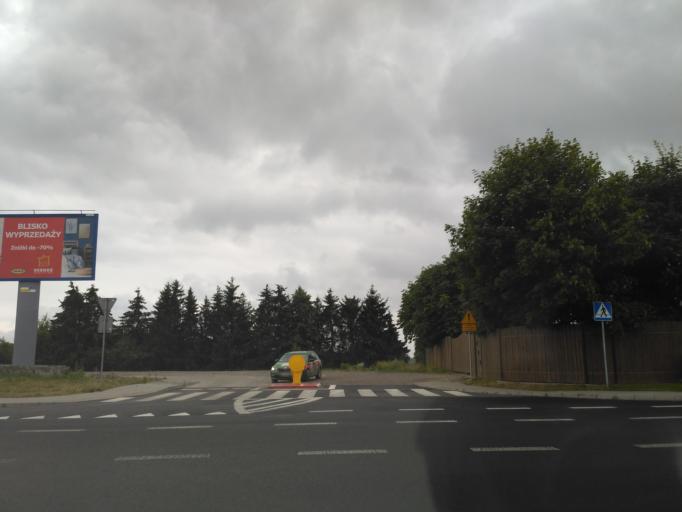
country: PL
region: Lublin Voivodeship
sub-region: Powiat lubelski
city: Lublin
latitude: 51.2810
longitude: 22.5683
